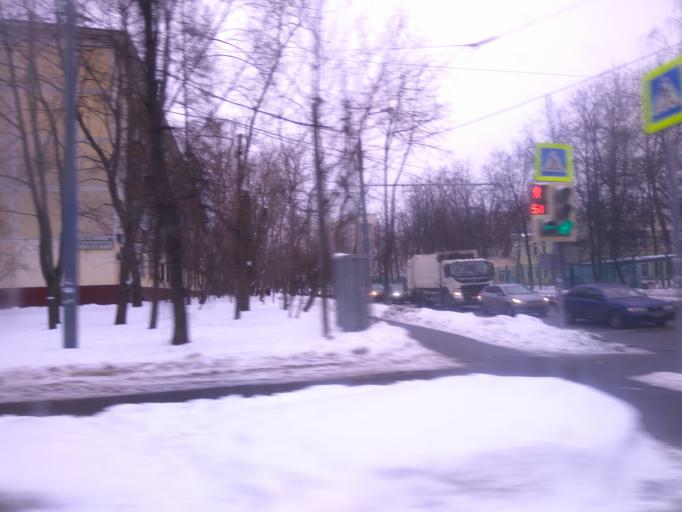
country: RU
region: Moskovskaya
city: Izmaylovo
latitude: 55.7973
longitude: 37.8189
